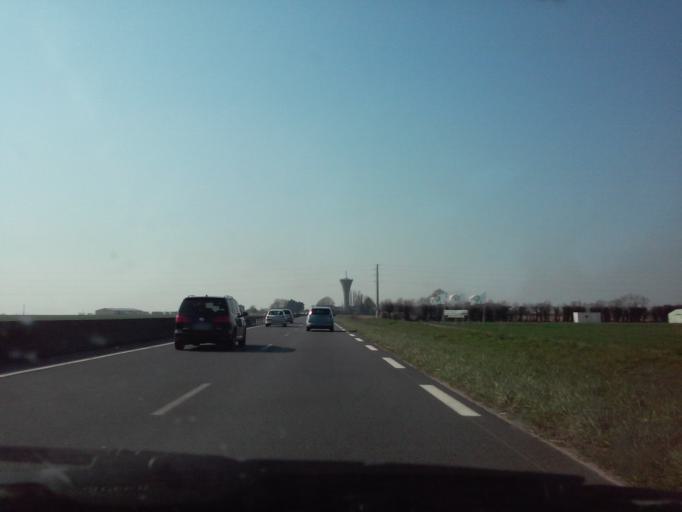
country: FR
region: Lower Normandy
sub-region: Departement du Calvados
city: Creully
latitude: 49.2371
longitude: -0.5893
